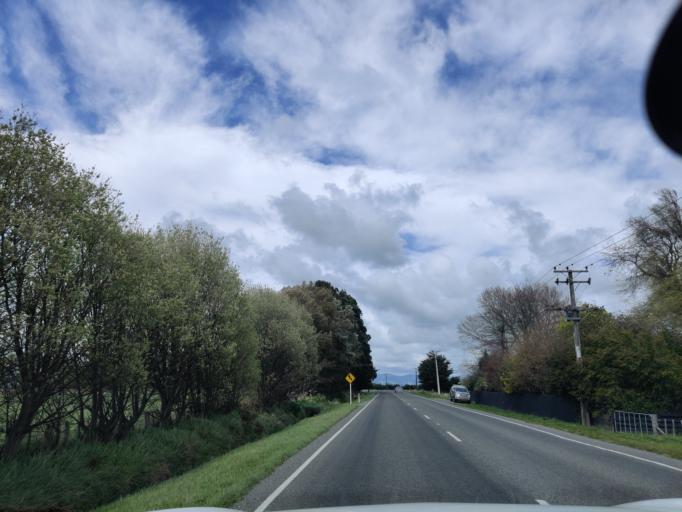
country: NZ
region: Manawatu-Wanganui
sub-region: Palmerston North City
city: Palmerston North
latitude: -40.3265
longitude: 175.5060
